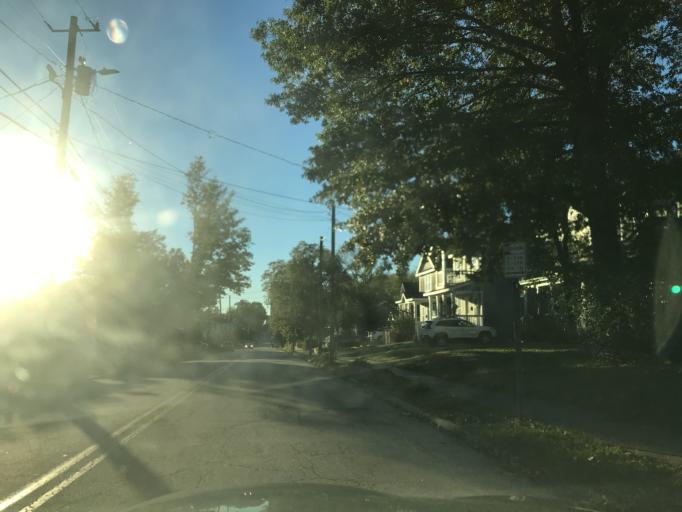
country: US
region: North Carolina
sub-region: Wake County
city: Raleigh
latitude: 35.7778
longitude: -78.6238
